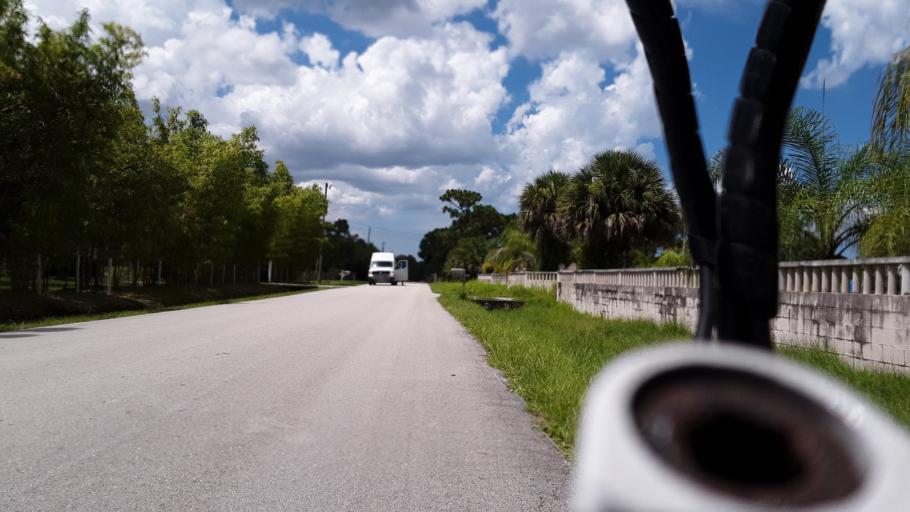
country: US
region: Florida
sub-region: Brevard County
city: Malabar
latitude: 27.9877
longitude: -80.5753
